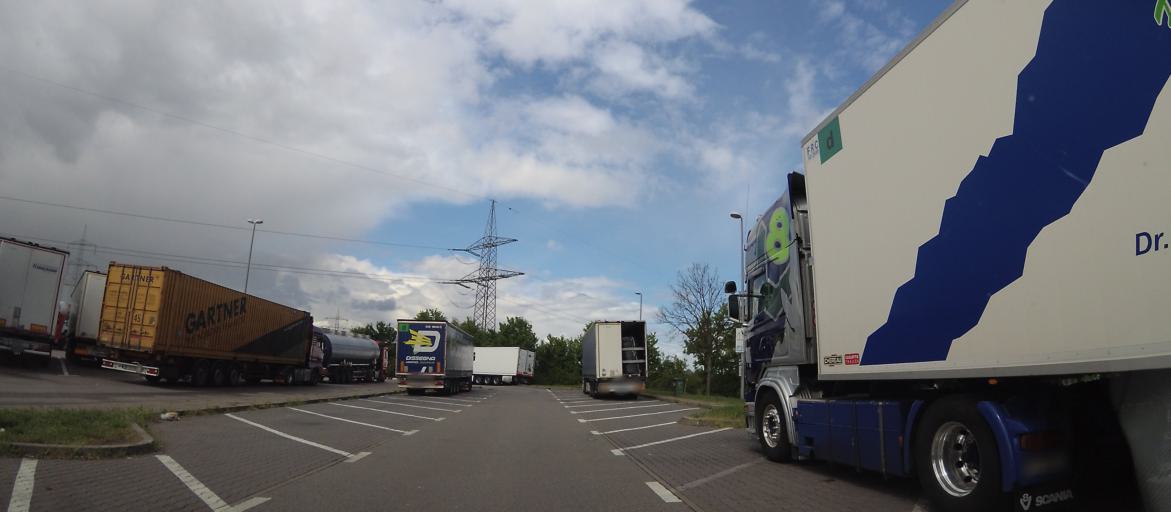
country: DE
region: Rheinland-Pfalz
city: Mutterstadt
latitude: 49.4109
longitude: 8.3415
